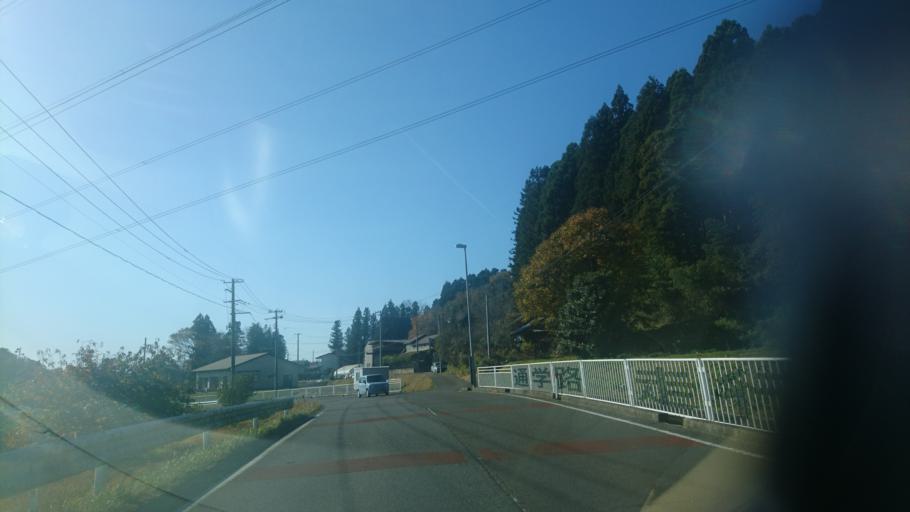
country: JP
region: Miyagi
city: Tomiya
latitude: 38.3991
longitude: 140.8665
